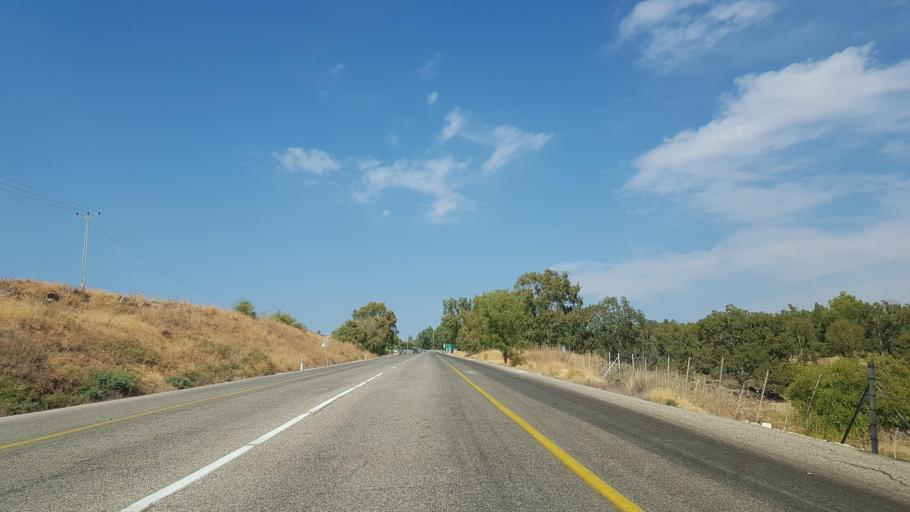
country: SY
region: Quneitra
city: Al Butayhah
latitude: 32.9081
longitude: 35.5972
